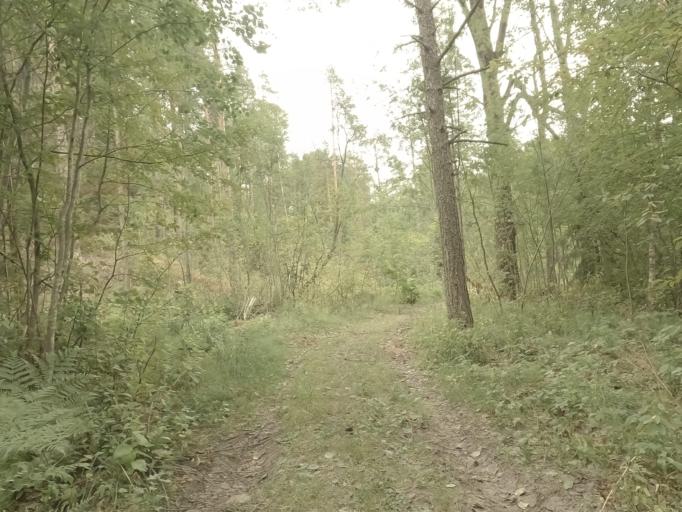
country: RU
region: Leningrad
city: Kamennogorsk
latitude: 61.0743
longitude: 29.1577
